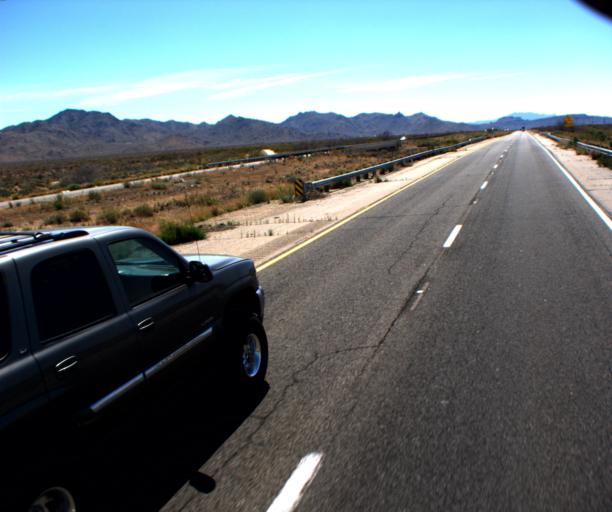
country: US
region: Arizona
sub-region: Mohave County
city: Golden Valley
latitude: 35.3041
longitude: -114.1924
